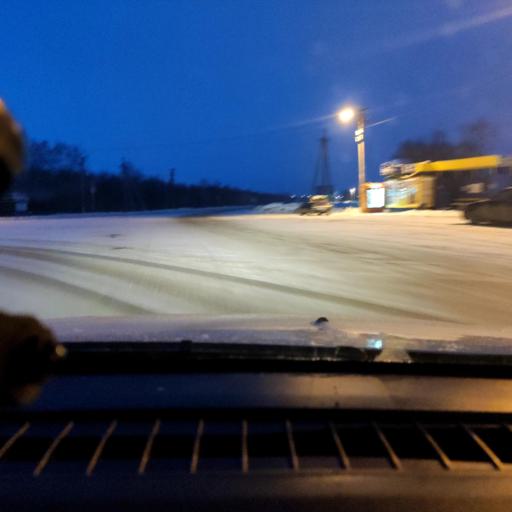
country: RU
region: Samara
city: Kinel'-Cherkassy
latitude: 53.4470
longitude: 51.5094
